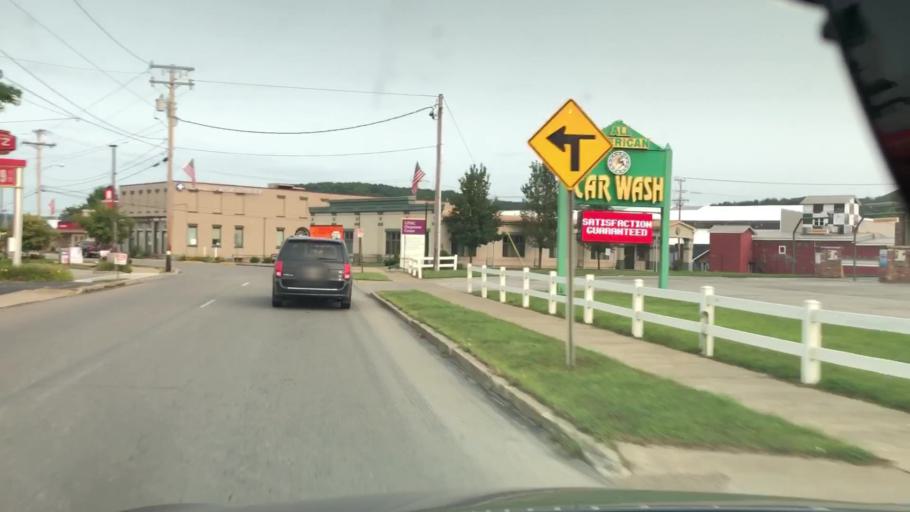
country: US
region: Pennsylvania
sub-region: Crawford County
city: Titusville
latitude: 41.6267
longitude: -79.6801
